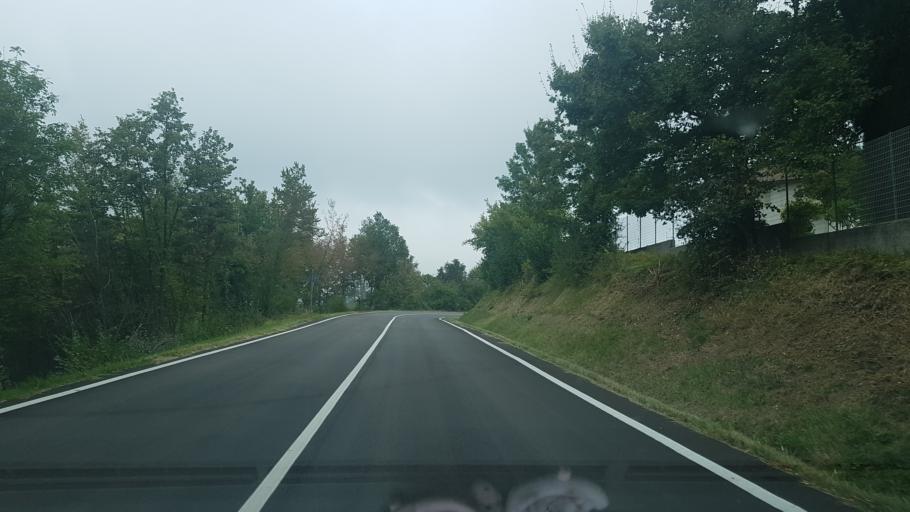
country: IT
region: Piedmont
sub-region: Provincia di Cuneo
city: Paroldo
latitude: 44.4200
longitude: 8.0921
